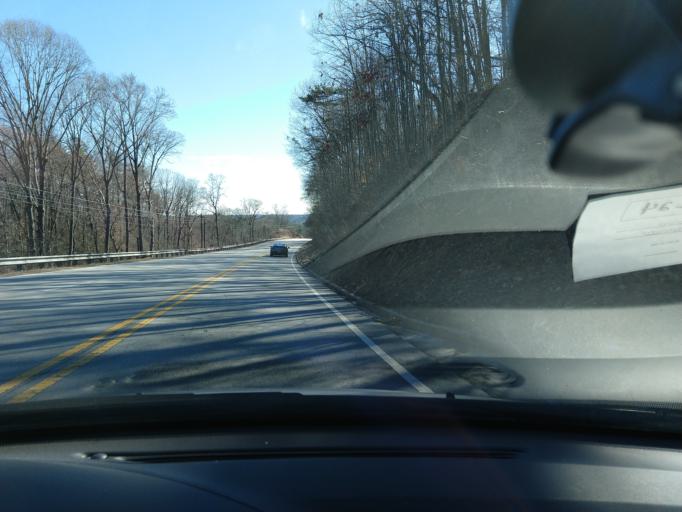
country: US
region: Georgia
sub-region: Stephens County
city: Toccoa
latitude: 34.6080
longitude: -83.3541
